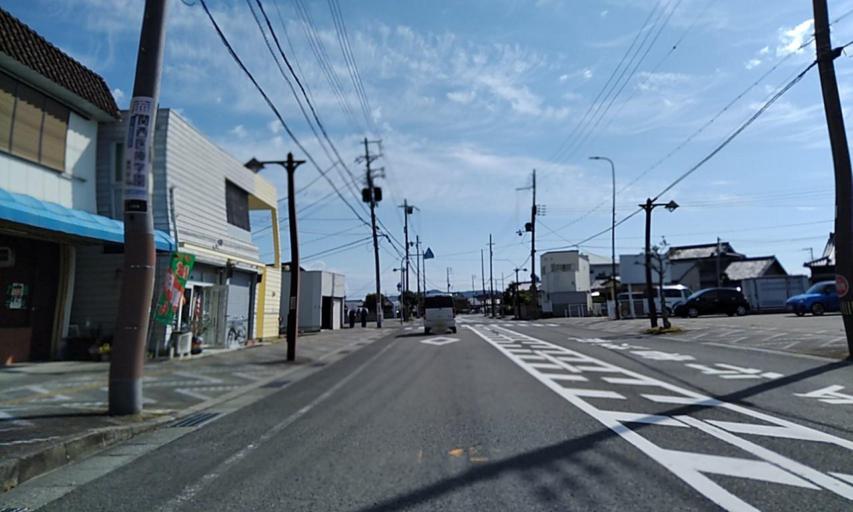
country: JP
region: Wakayama
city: Gobo
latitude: 33.9063
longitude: 135.1600
